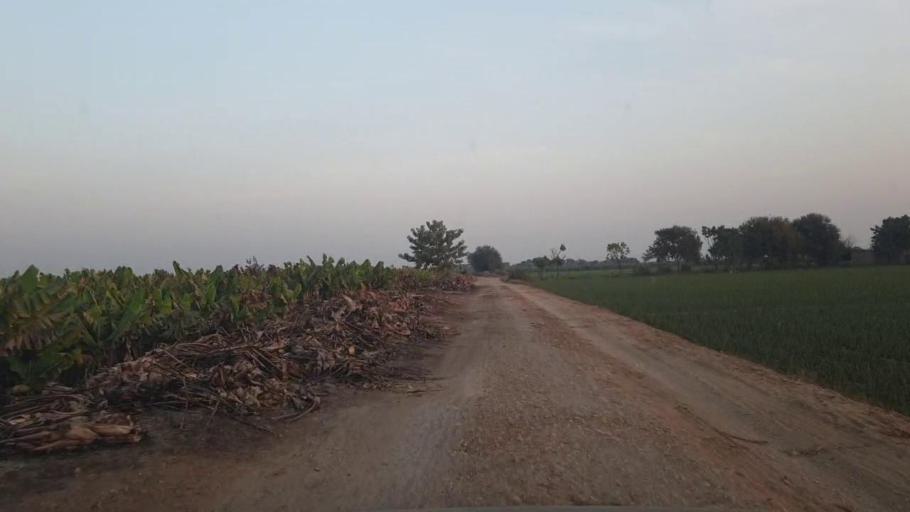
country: PK
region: Sindh
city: Bhit Shah
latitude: 25.8466
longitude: 68.5216
